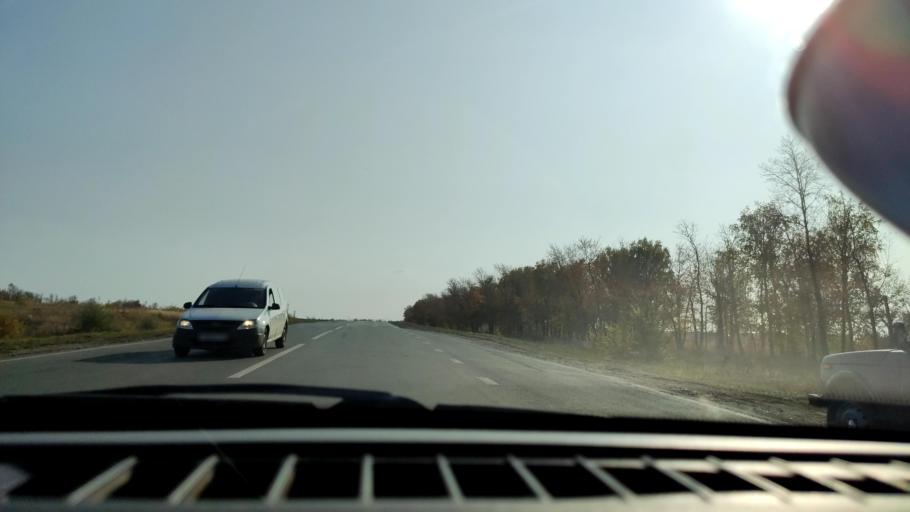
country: RU
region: Samara
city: Dubovyy Umet
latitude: 53.0932
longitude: 50.3495
